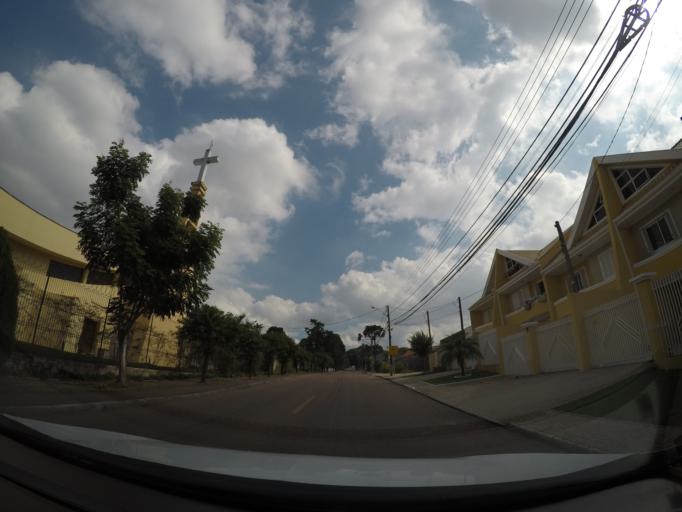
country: BR
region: Parana
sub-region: Curitiba
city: Curitiba
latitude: -25.4821
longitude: -49.2569
